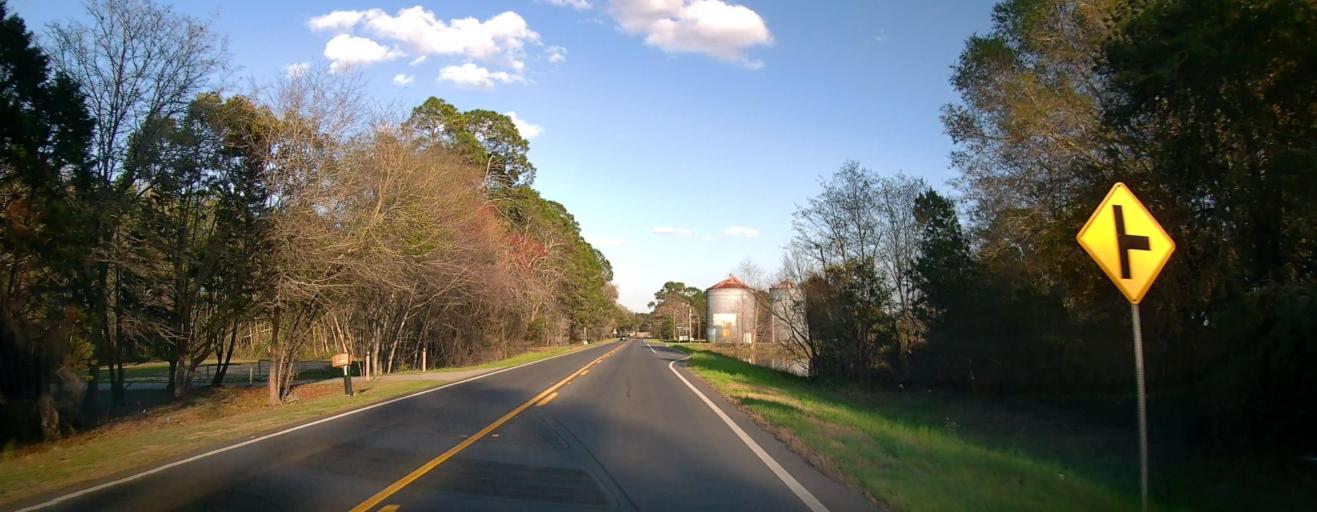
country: US
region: Georgia
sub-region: Evans County
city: Claxton
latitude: 32.1617
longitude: -81.8875
